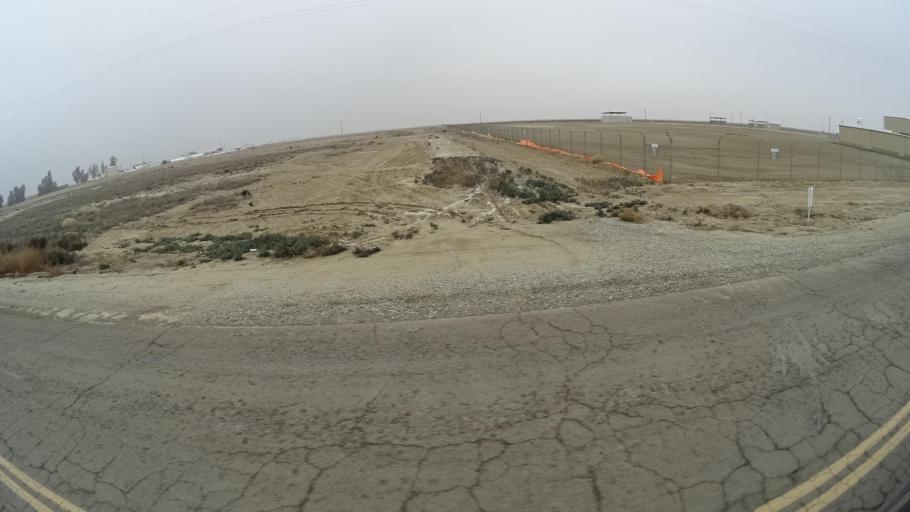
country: US
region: California
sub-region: Kern County
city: Maricopa
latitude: 35.1483
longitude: -119.2401
